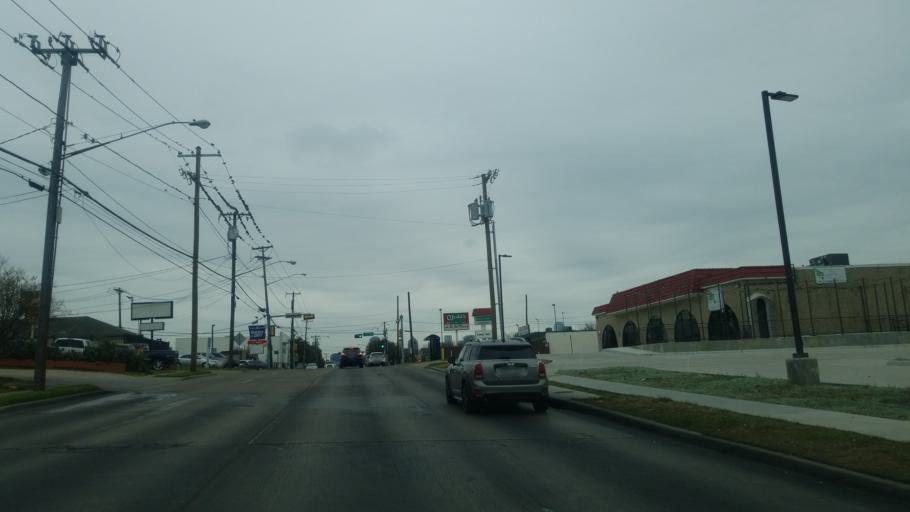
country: US
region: Texas
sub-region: Dallas County
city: Dallas
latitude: 32.8142
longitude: -96.8260
